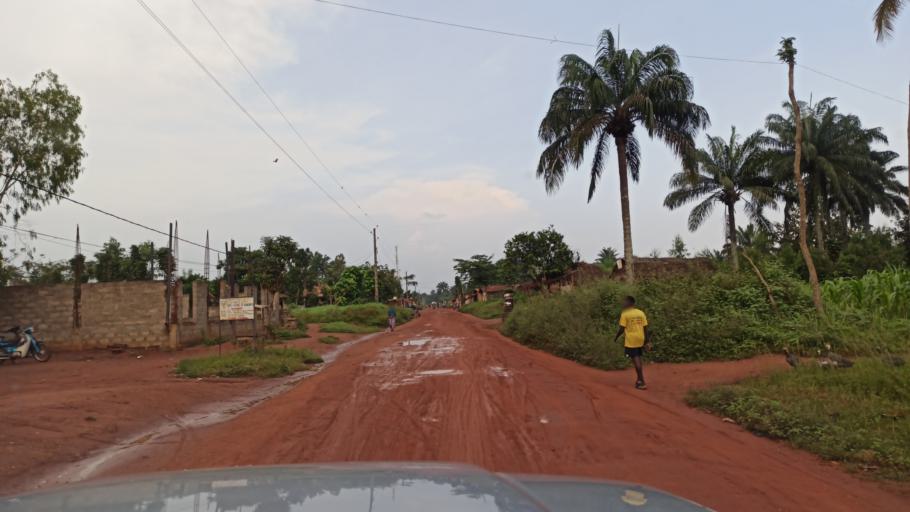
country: BJ
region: Queme
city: Porto-Novo
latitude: 6.4947
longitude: 2.6916
